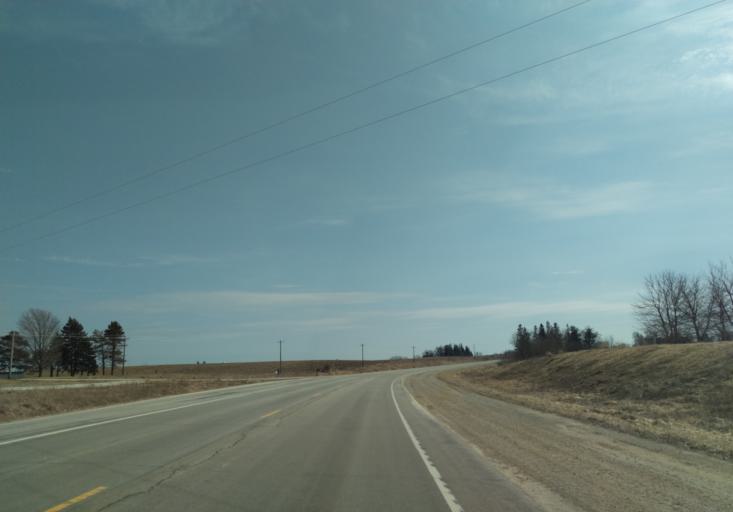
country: US
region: Iowa
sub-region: Winneshiek County
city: Decorah
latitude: 43.4505
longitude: -91.8644
